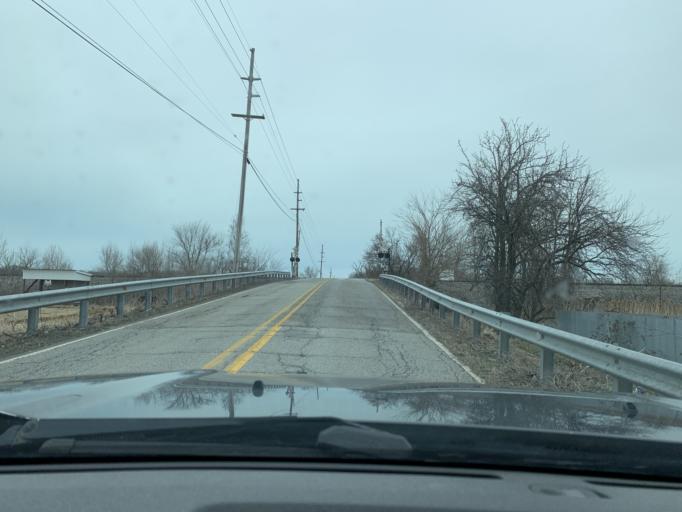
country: US
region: Indiana
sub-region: Porter County
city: Chesterton
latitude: 41.5650
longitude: -87.0664
